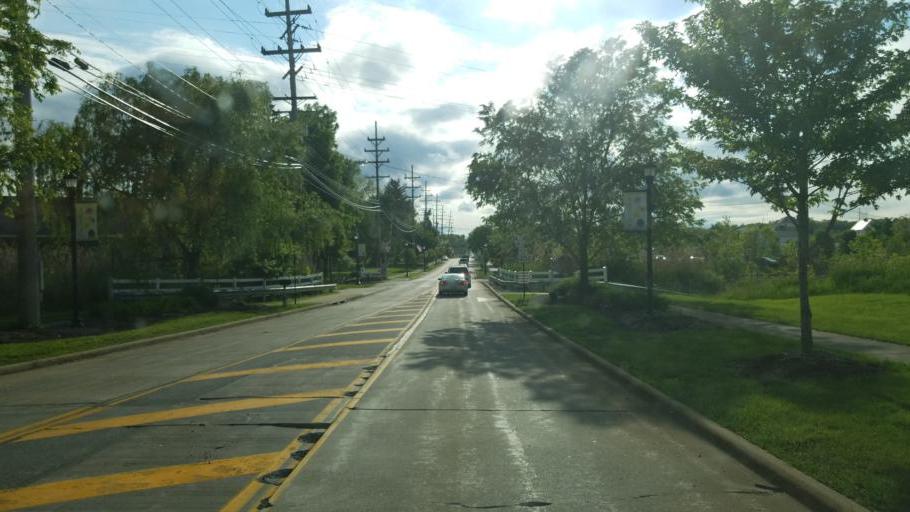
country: US
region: Ohio
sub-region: Cuyahoga County
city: Solon
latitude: 41.3569
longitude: -81.4660
